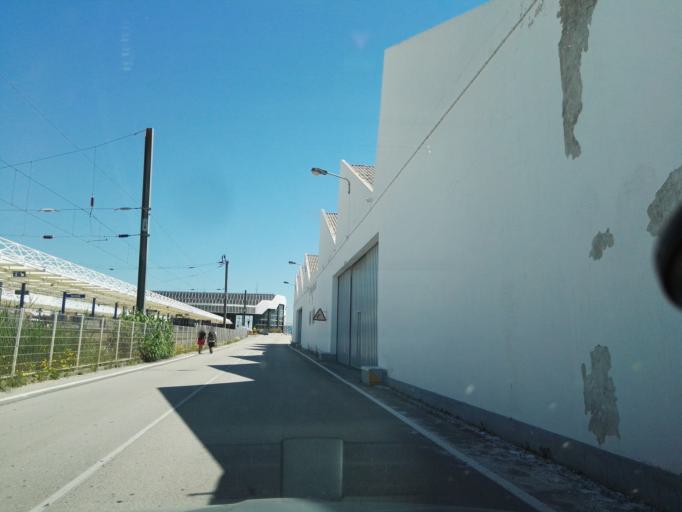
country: PT
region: Lisbon
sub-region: Vila Franca de Xira
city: Sobralinho
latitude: 38.8891
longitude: -9.0346
